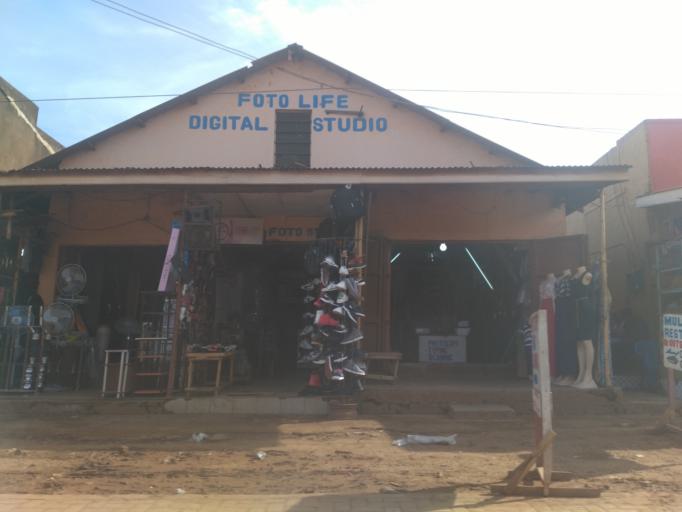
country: UG
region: Central Region
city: Kampala Central Division
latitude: 0.3527
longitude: 32.5616
